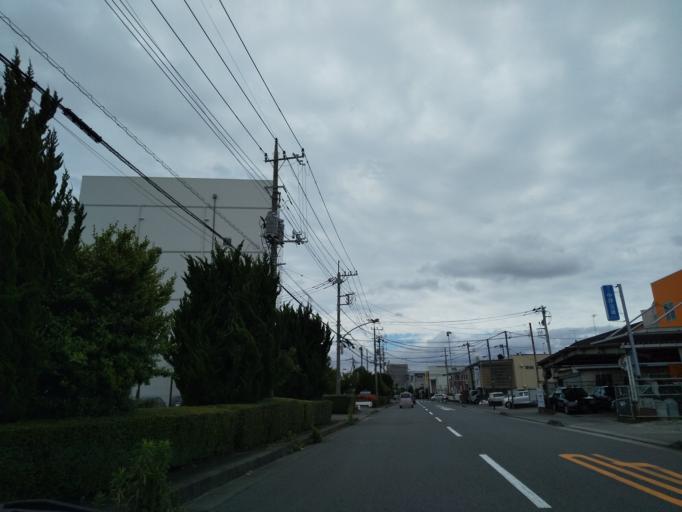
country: JP
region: Kanagawa
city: Zama
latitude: 35.5203
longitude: 139.3390
